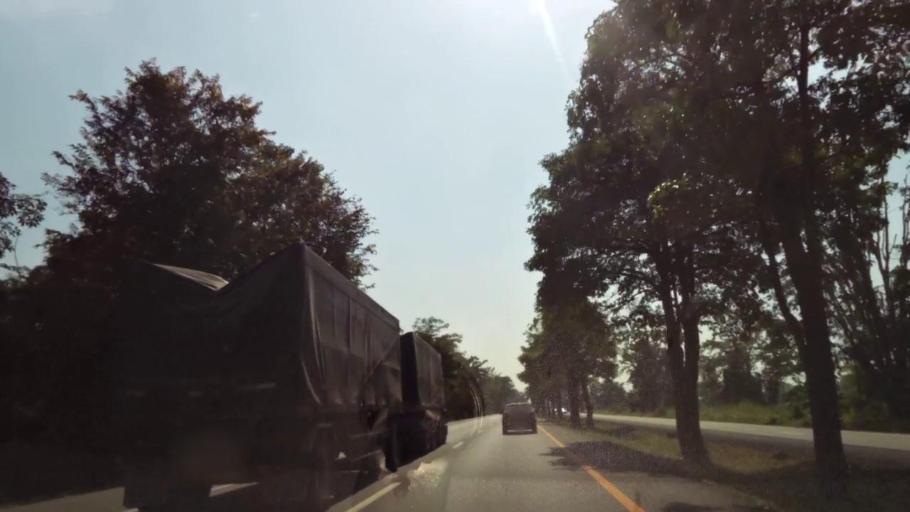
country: TH
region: Phichit
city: Bueng Na Rang
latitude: 16.0520
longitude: 100.1211
